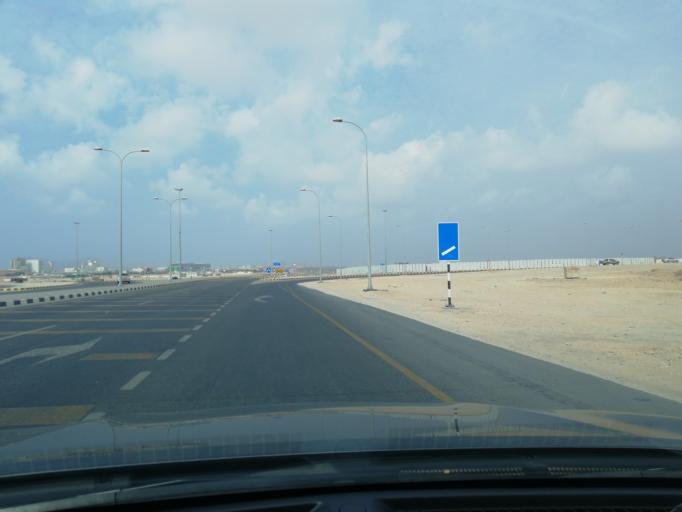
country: OM
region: Zufar
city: Salalah
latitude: 16.9490
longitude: 53.9886
